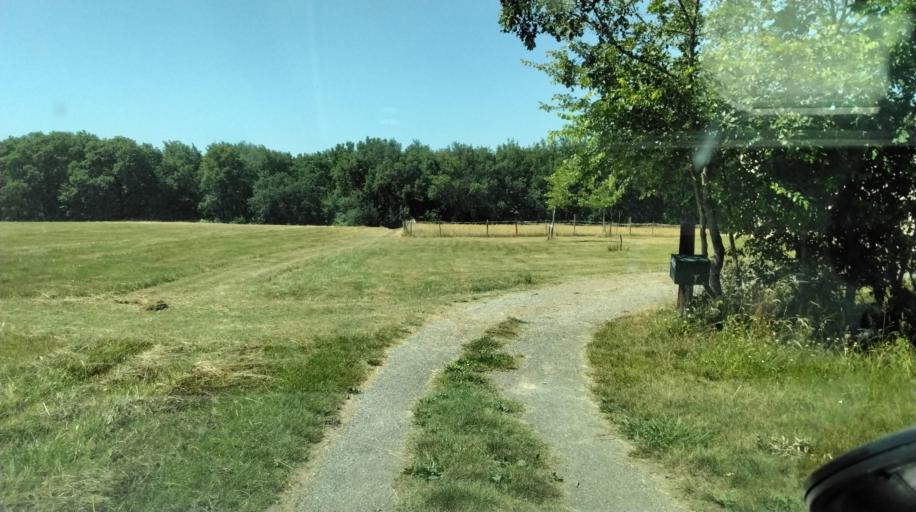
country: FR
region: Midi-Pyrenees
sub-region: Departement de la Haute-Garonne
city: Sainte-Foy-de-Peyrolieres
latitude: 43.4791
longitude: 1.1269
